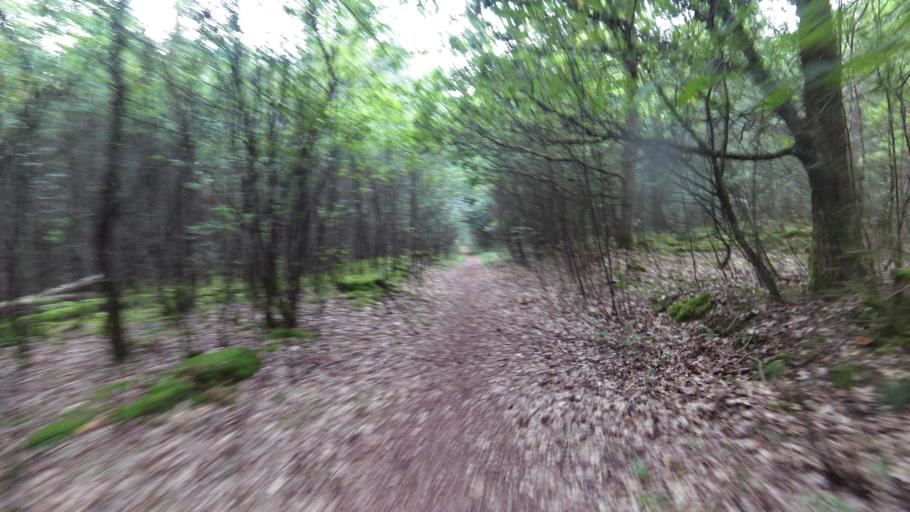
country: NL
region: Gelderland
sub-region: Gemeente Renkum
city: Renkum
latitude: 51.9895
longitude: 5.7226
